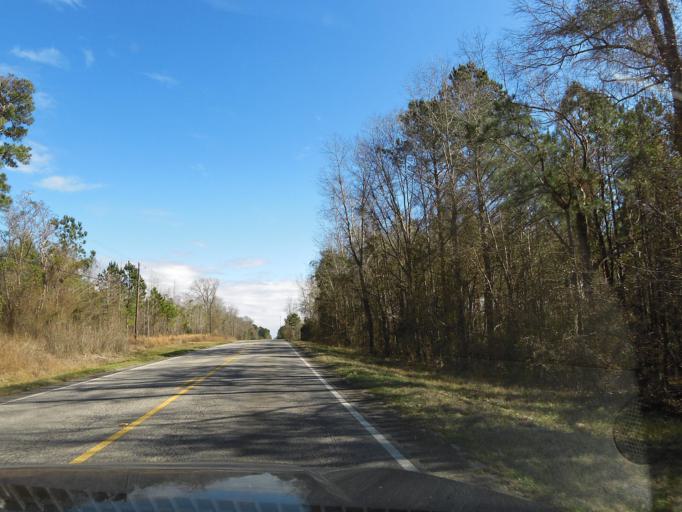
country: US
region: Alabama
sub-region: Barbour County
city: Clayton
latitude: 32.0314
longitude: -85.3634
